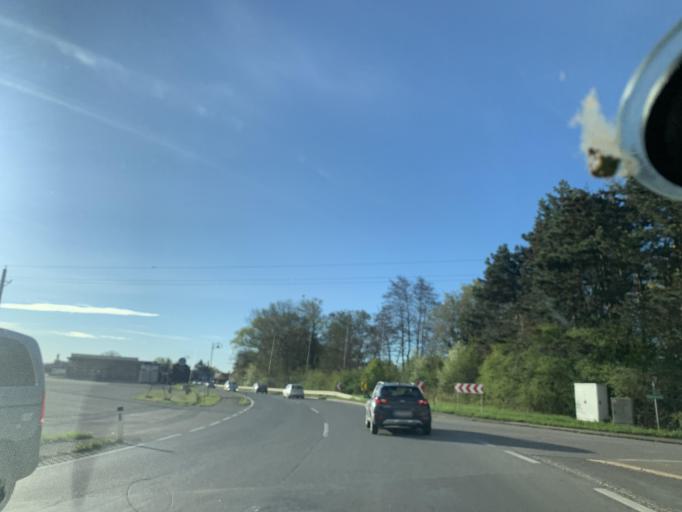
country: AT
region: Styria
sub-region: Politischer Bezirk Leibnitz
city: Kaindorf an der Sulm
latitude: 46.8064
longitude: 15.5308
